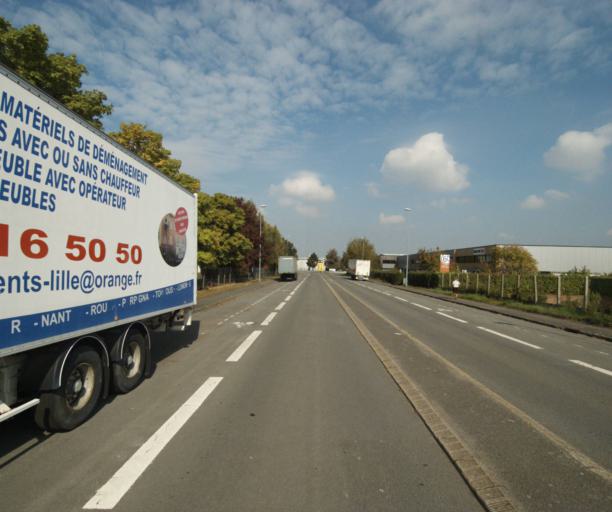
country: FR
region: Nord-Pas-de-Calais
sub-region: Departement du Nord
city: Wattignies
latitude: 50.5729
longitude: 3.0313
